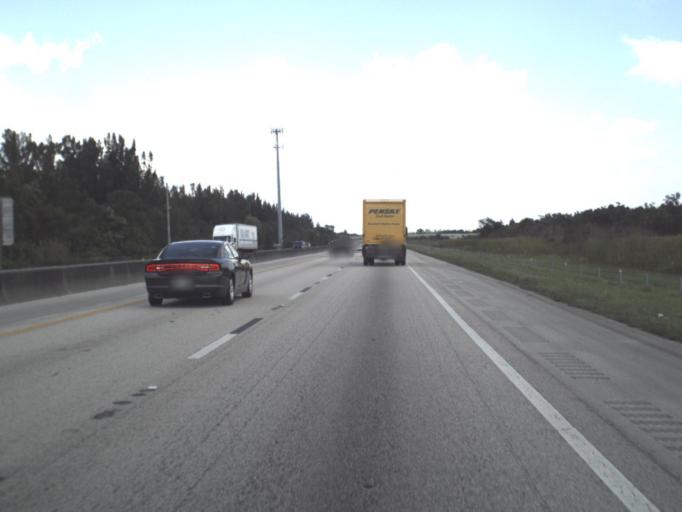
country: US
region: Florida
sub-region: Palm Beach County
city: Schall Circle
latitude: 26.7274
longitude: -80.1354
